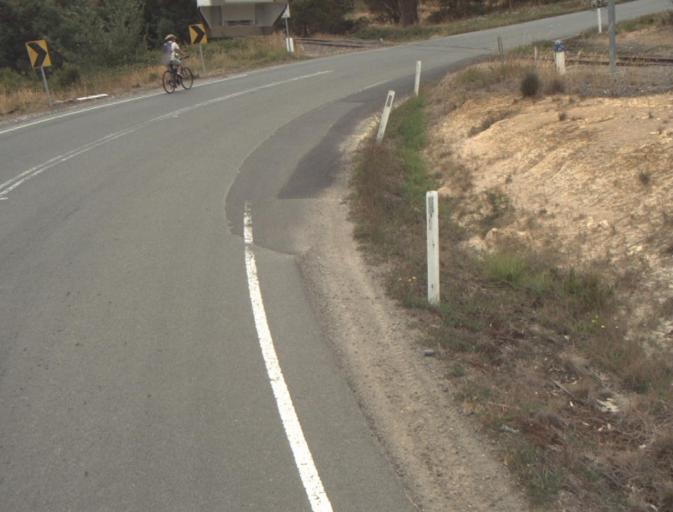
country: AU
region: Tasmania
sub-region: Launceston
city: Mayfield
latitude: -41.2254
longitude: 147.2065
